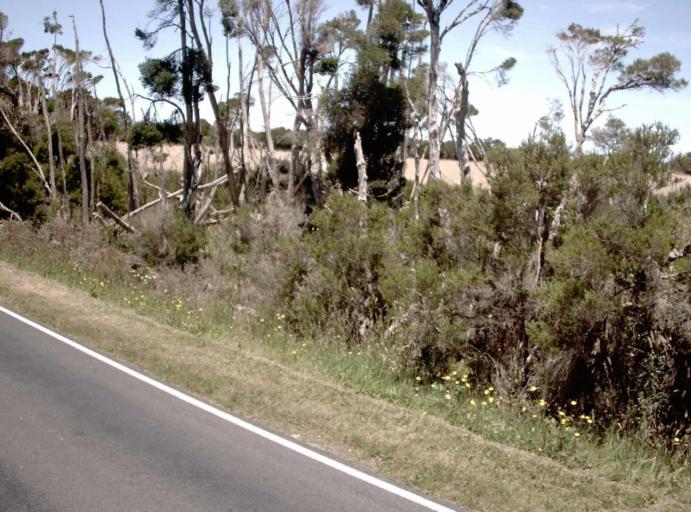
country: AU
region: Victoria
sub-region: Bass Coast
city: North Wonthaggi
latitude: -38.7754
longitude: 146.1617
